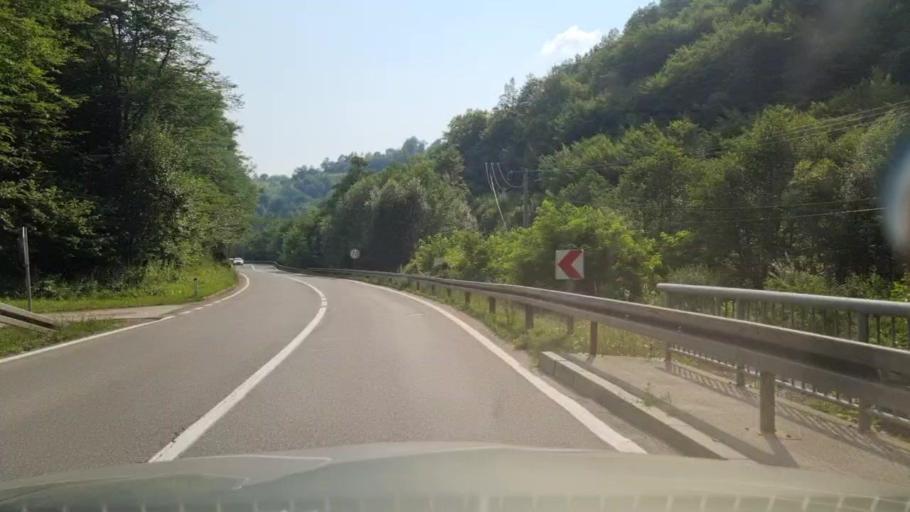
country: BA
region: Federation of Bosnia and Herzegovina
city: Hotonj
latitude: 43.9830
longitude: 18.3946
